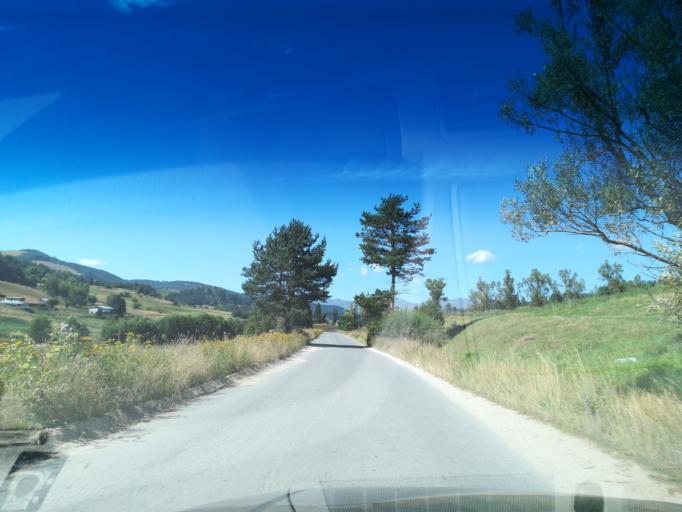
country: BG
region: Sofiya
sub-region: Obshtina Koprivshtitsa
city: Koprivshtitsa
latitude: 42.6100
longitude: 24.3763
